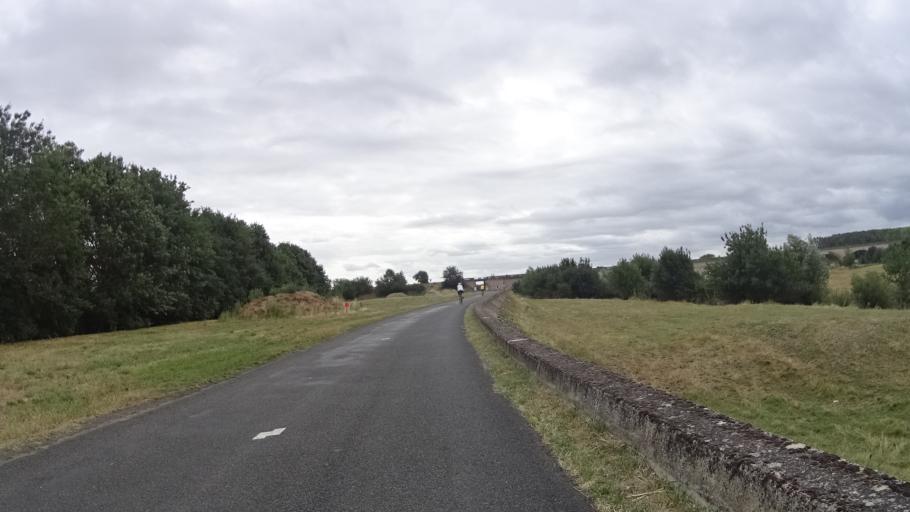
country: FR
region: Pays de la Loire
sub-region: Departement de Maine-et-Loire
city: La Possonniere
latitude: 47.3646
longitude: -0.7228
